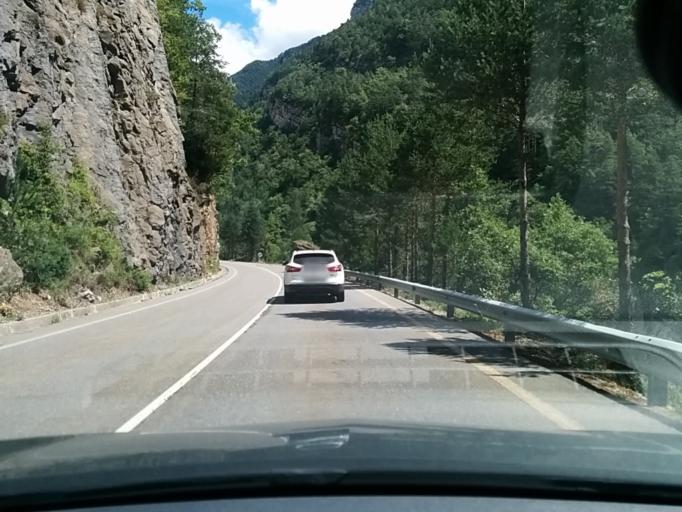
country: ES
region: Aragon
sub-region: Provincia de Huesca
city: Bielsa
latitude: 42.5891
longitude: 0.2308
